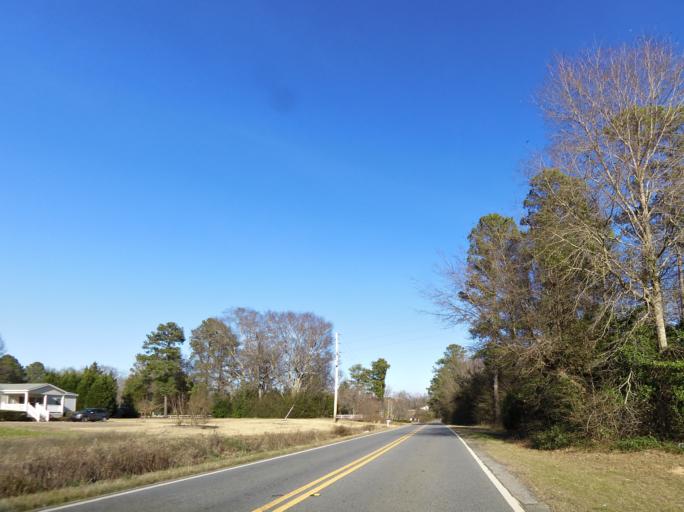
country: US
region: Georgia
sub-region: Bibb County
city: West Point
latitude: 32.7744
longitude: -83.8268
